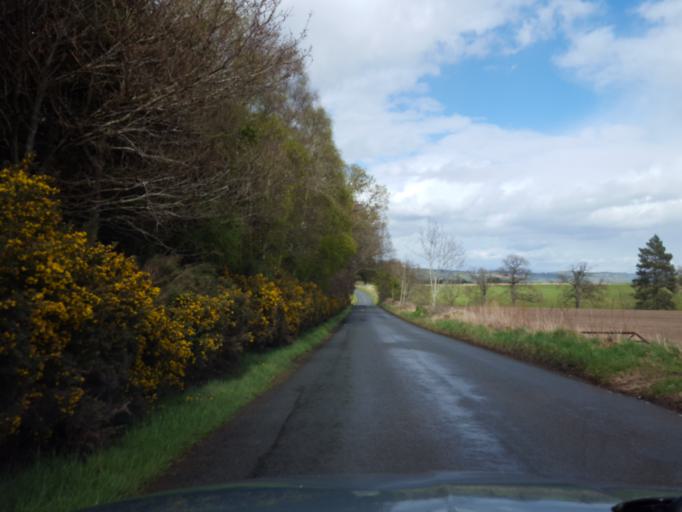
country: GB
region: Scotland
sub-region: Perth and Kinross
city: Methven
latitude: 56.3204
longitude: -3.5783
